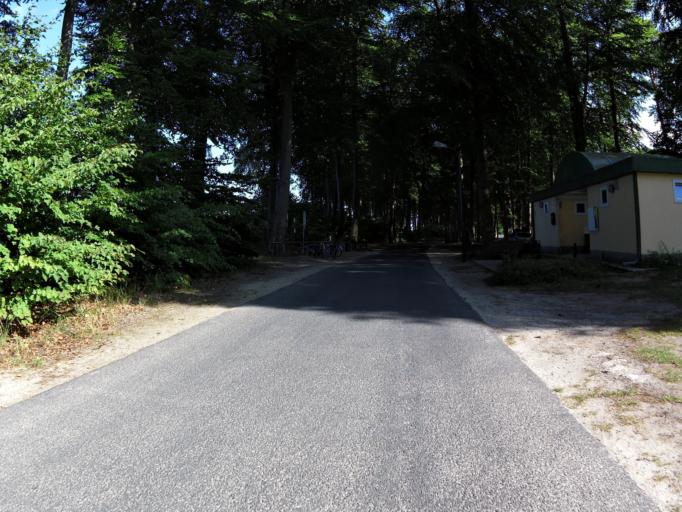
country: DE
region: Mecklenburg-Vorpommern
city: Seebad Bansin
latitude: 53.9998
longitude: 14.1004
